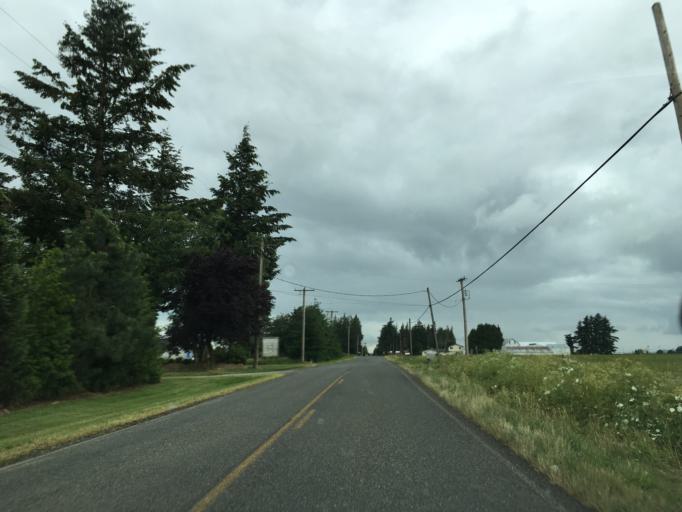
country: US
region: Washington
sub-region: Whatcom County
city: Lynden
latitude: 48.9786
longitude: -122.3895
